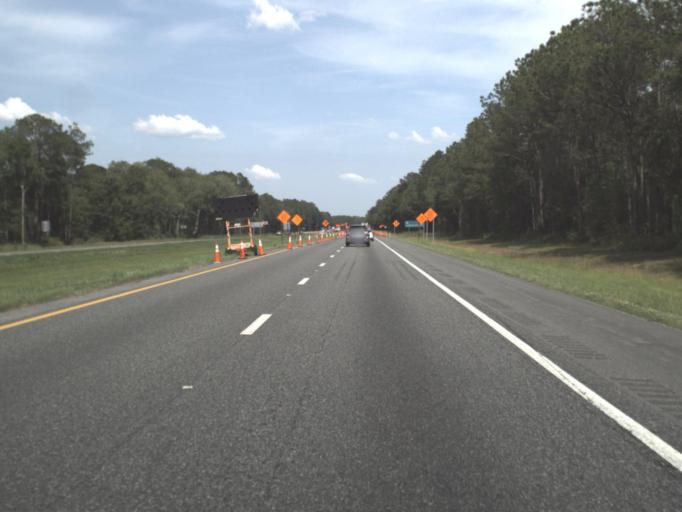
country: US
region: Florida
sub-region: Columbia County
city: Five Points
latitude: 30.2412
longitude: -82.6250
